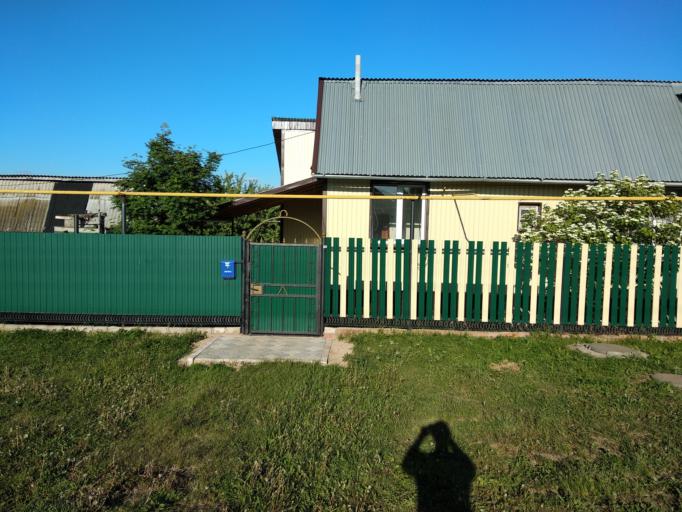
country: RU
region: Tatarstan
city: Nurlat
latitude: 54.8388
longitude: 50.7849
